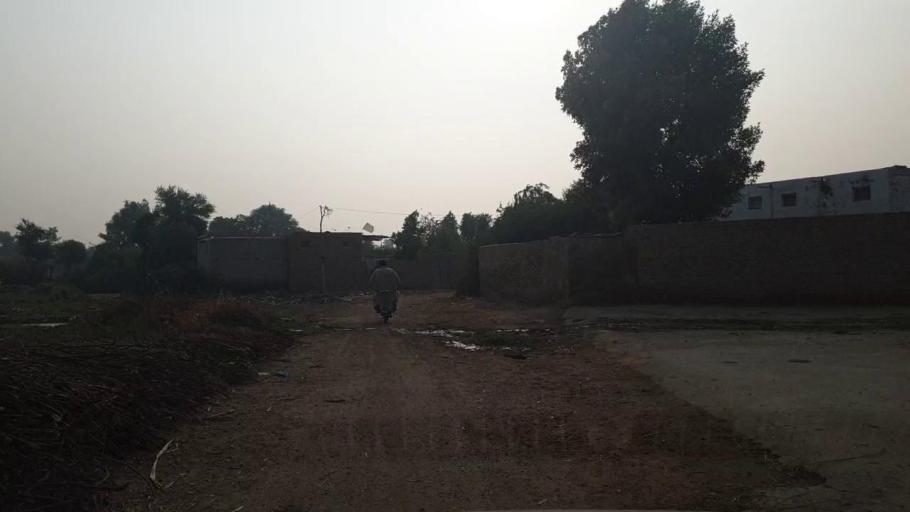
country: PK
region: Sindh
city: Hyderabad
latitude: 25.3737
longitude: 68.4140
